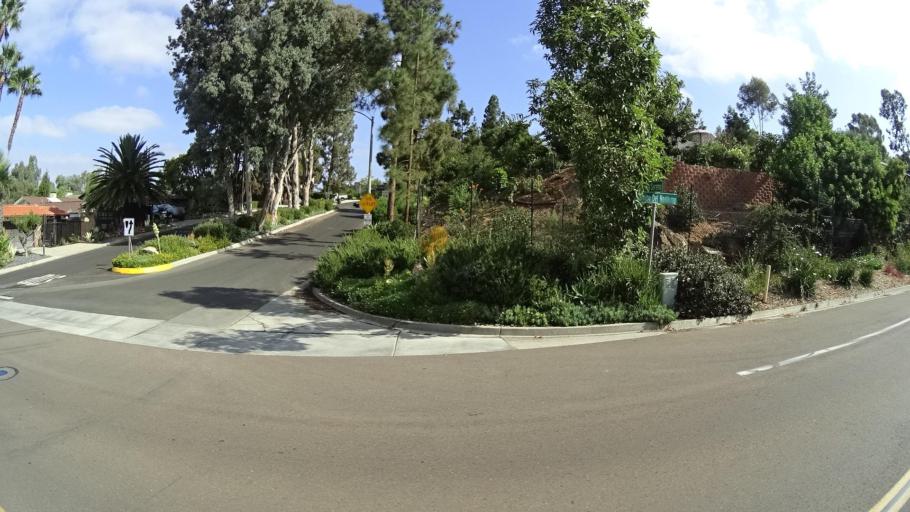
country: US
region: California
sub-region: San Diego County
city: Rancho Santa Fe
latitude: 33.0476
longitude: -117.2237
